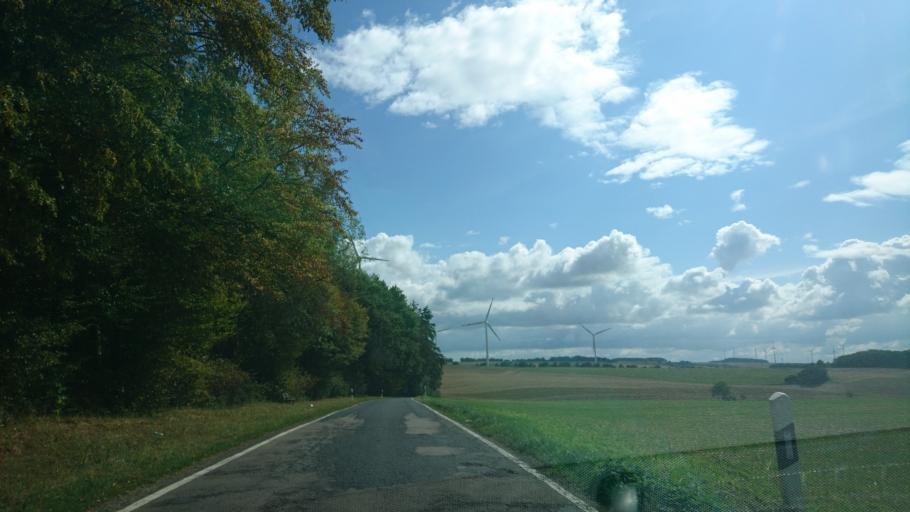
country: DE
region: Rheinland-Pfalz
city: Merzkirchen
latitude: 49.5697
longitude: 6.4643
